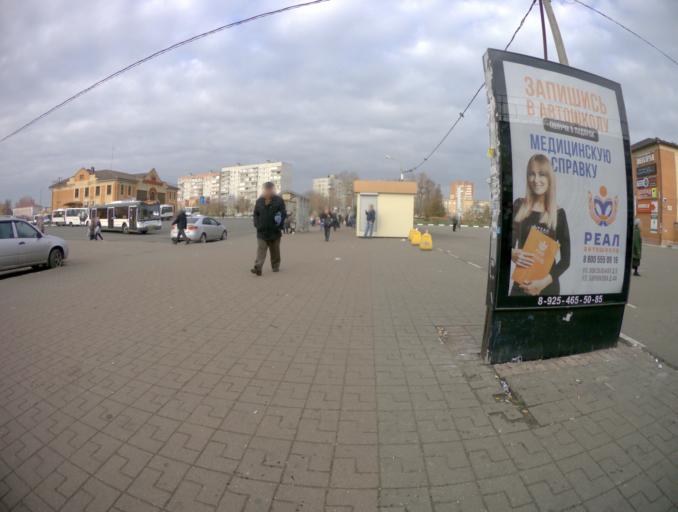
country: RU
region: Moskovskaya
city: Orekhovo-Zuyevo
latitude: 55.7956
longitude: 38.9750
